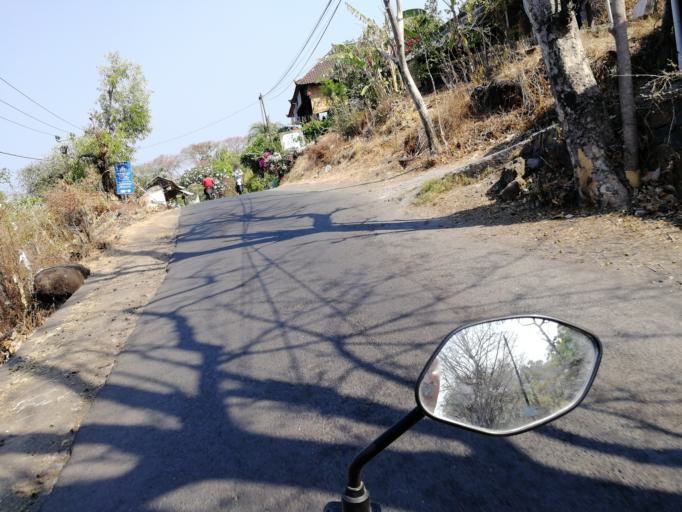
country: ID
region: Bali
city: Biaslantang Kaler
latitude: -8.3420
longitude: 115.6671
